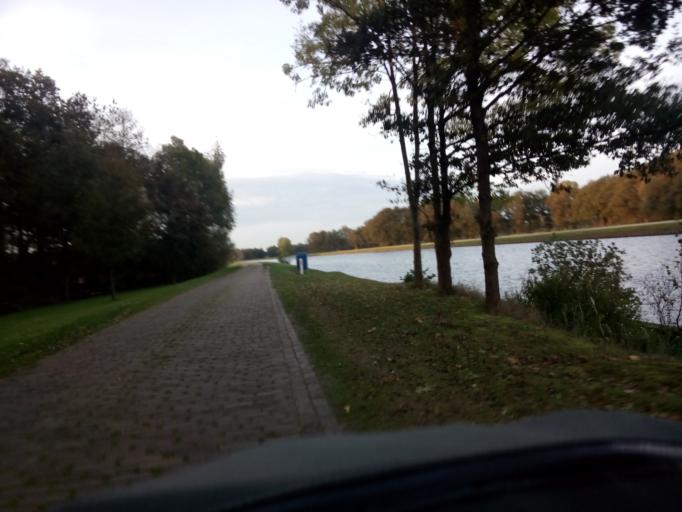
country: NL
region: Drenthe
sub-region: Gemeente Tynaarlo
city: Tynaarlo
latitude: 53.0498
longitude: 6.6078
